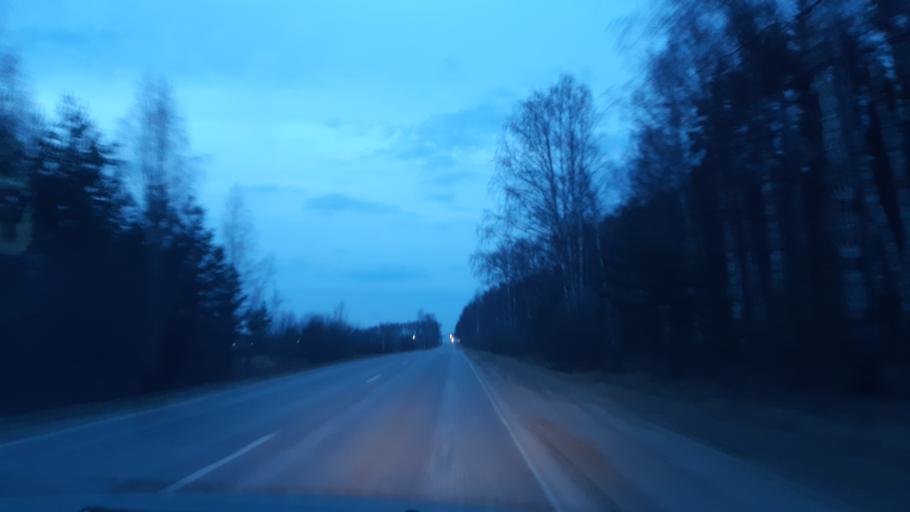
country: RU
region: Vladimir
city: Luknovo
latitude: 56.2284
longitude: 42.0348
